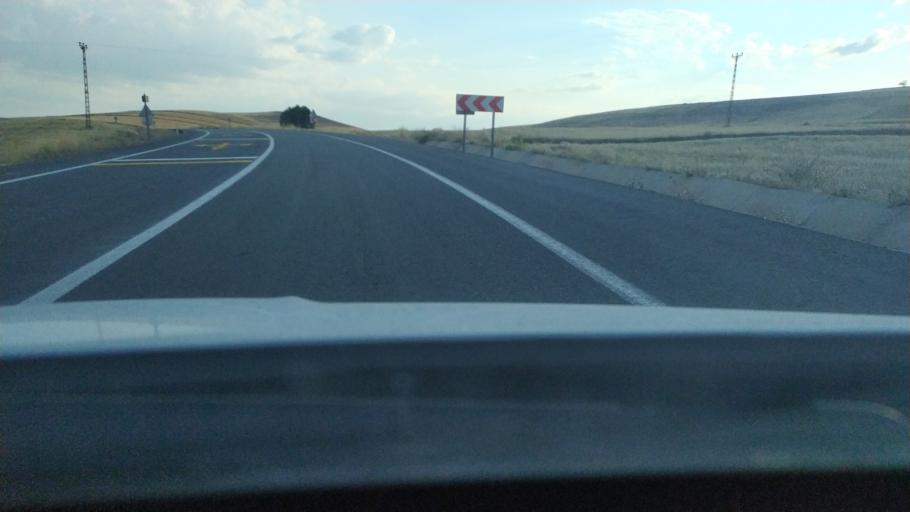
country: TR
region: Kayseri
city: Muncusun
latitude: 38.9536
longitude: 35.7518
